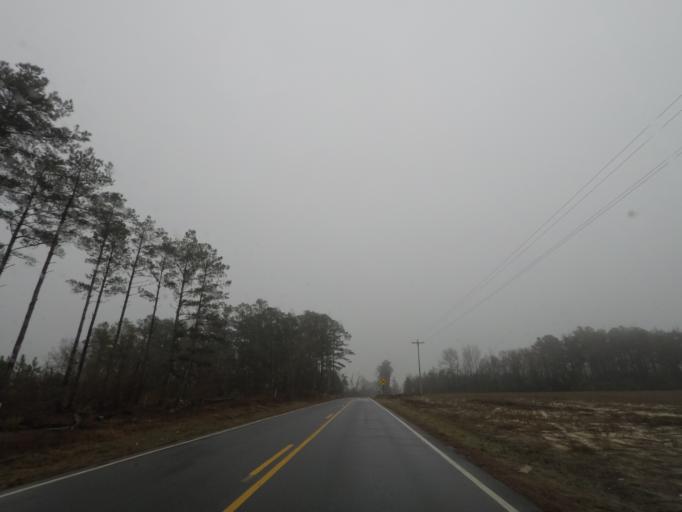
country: US
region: North Carolina
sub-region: Scotland County
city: Laurinburg
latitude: 34.8112
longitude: -79.4469
